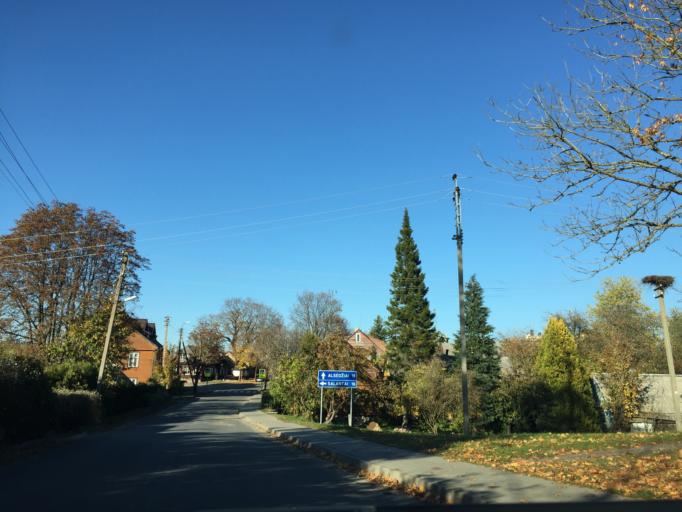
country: LT
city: Plateliai
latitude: 56.0411
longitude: 21.8155
